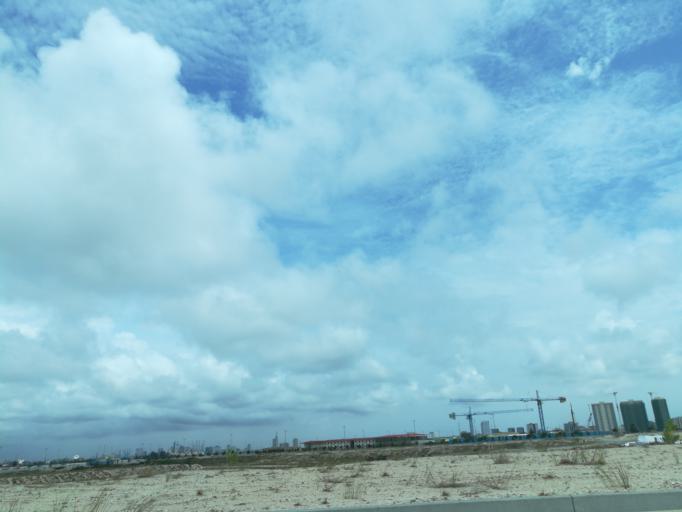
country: NG
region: Lagos
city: Lagos
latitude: 6.4078
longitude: 3.4064
